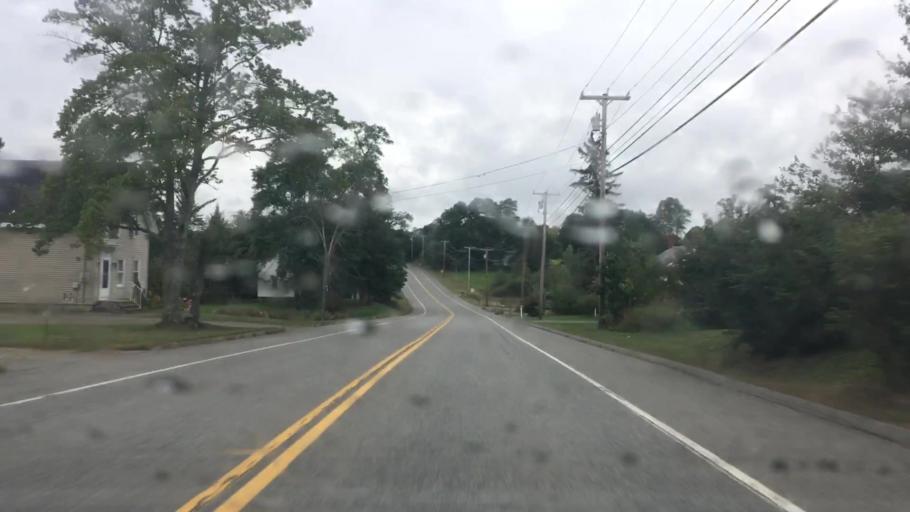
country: US
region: Maine
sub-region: Penobscot County
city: Orrington
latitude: 44.7188
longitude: -68.8266
